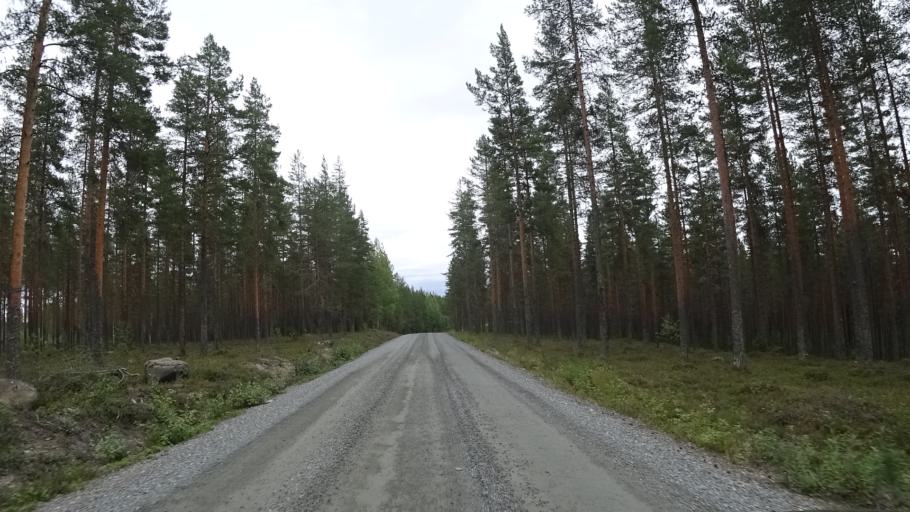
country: FI
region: North Karelia
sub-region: Pielisen Karjala
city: Lieksa
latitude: 63.3736
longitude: 30.3706
